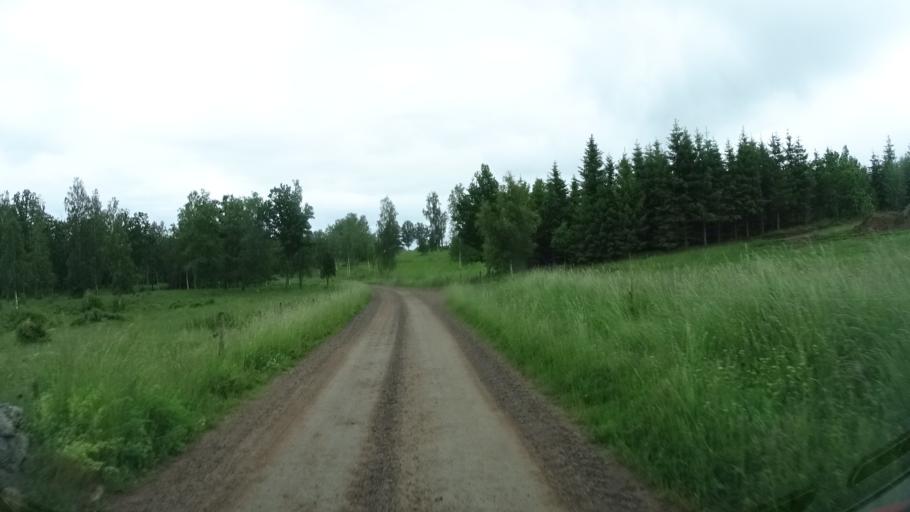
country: SE
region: Joenkoeping
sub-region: Eksjo Kommun
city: Mariannelund
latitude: 57.6158
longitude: 15.6652
